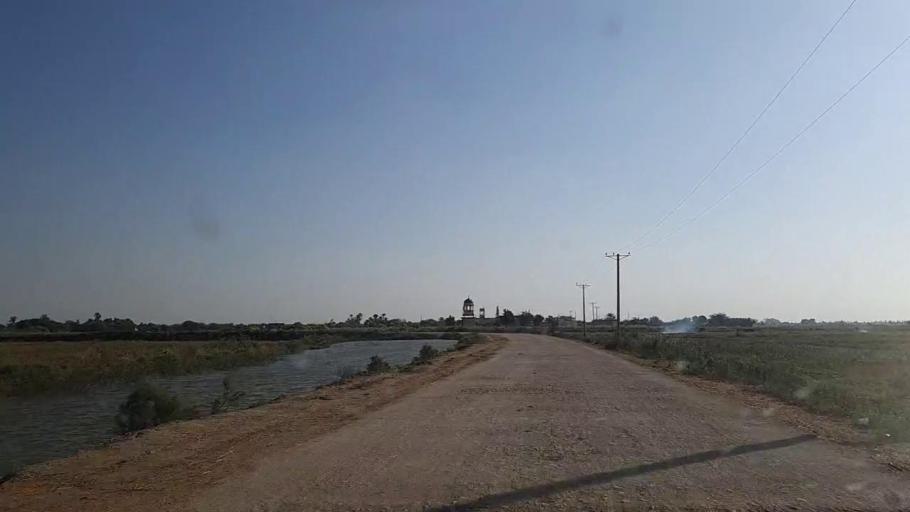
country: PK
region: Sindh
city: Daro Mehar
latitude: 24.6288
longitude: 68.0790
